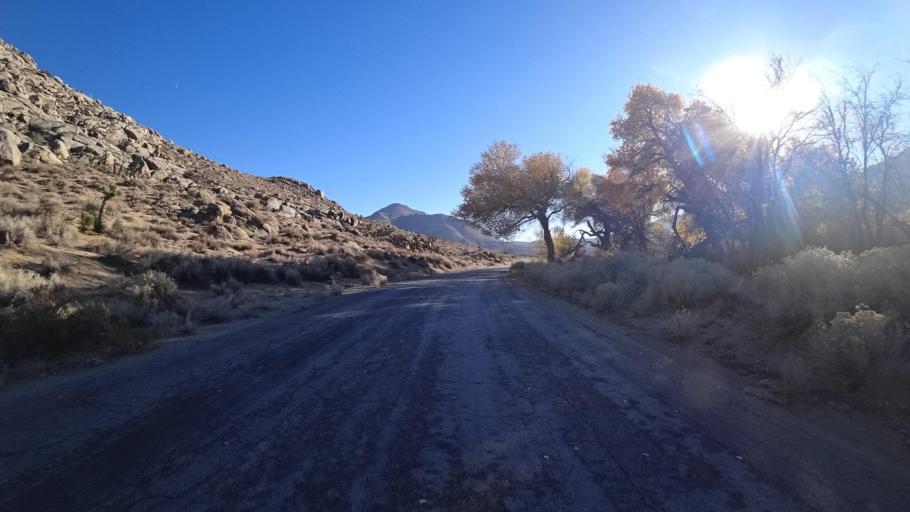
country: US
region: California
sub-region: Kern County
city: Weldon
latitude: 35.4998
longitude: -118.2039
